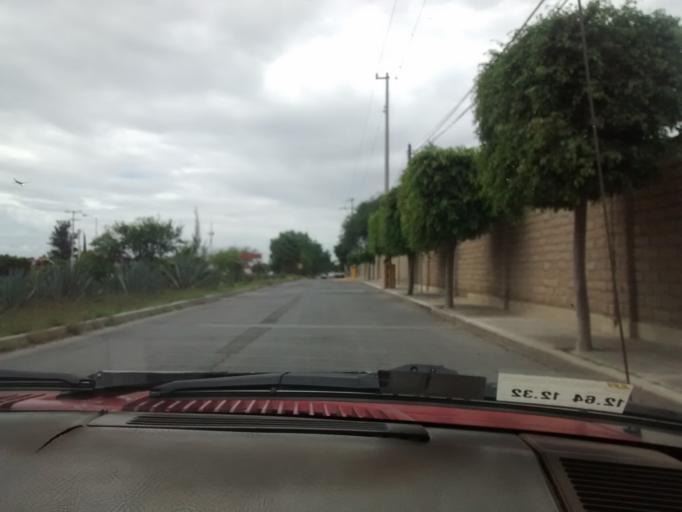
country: MX
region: Puebla
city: Tehuacan
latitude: 18.4803
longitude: -97.4118
